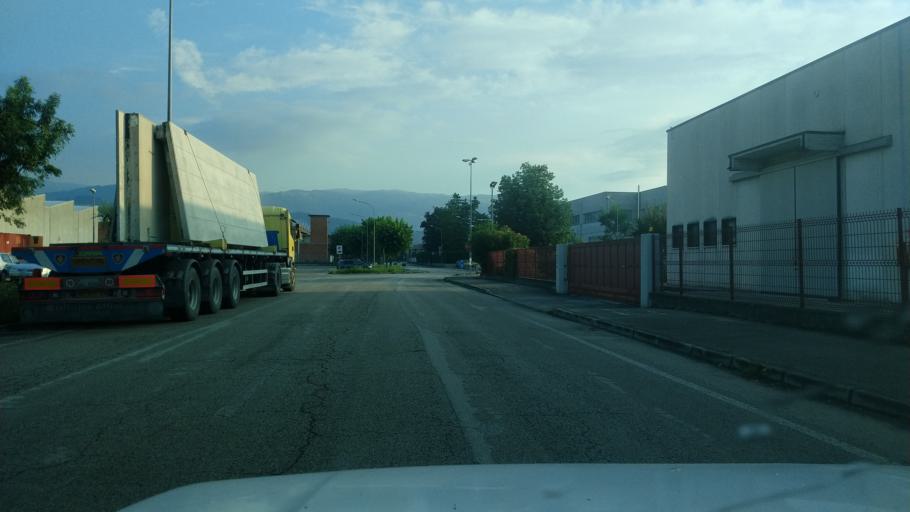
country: IT
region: Veneto
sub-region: Provincia di Vicenza
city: Schiavon
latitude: 45.7184
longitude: 11.6454
